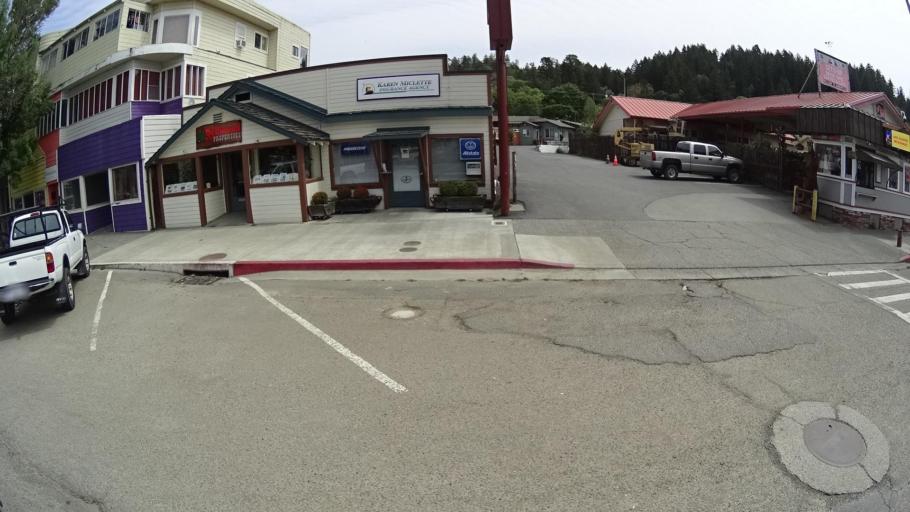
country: US
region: California
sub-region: Humboldt County
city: Redway
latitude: 40.0995
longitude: -123.7950
